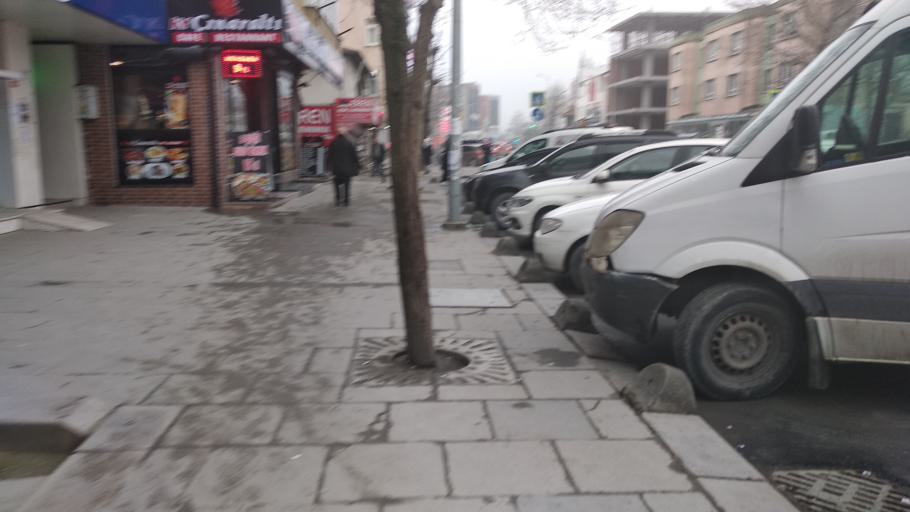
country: TR
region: Istanbul
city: Basaksehir
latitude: 41.1821
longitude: 28.7434
